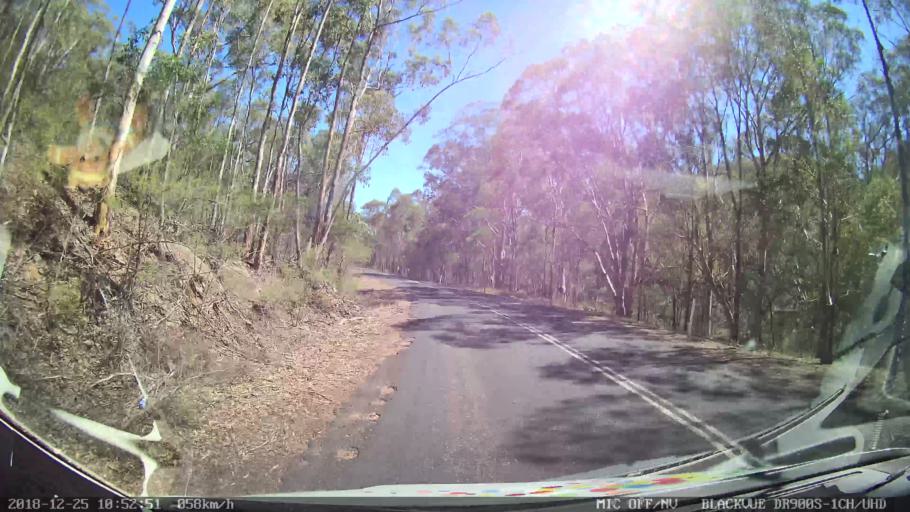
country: AU
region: New South Wales
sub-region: Upper Hunter Shire
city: Merriwa
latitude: -32.4250
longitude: 150.2740
